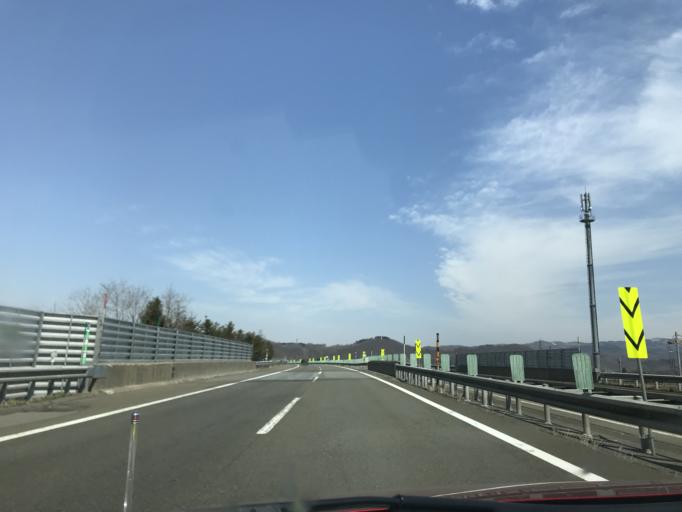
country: JP
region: Hokkaido
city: Iwamizawa
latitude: 43.2244
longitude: 141.8298
